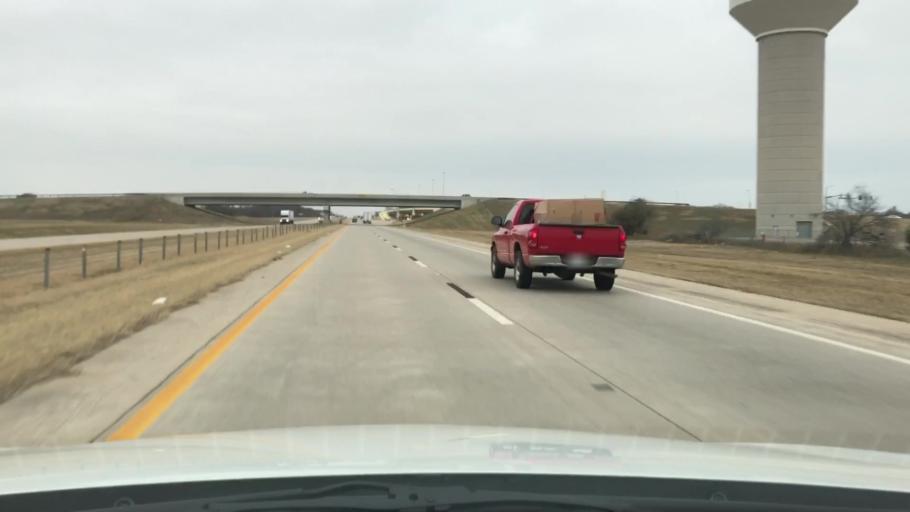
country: US
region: Texas
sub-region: Cooke County
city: Gainesville
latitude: 33.7640
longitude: -97.1348
